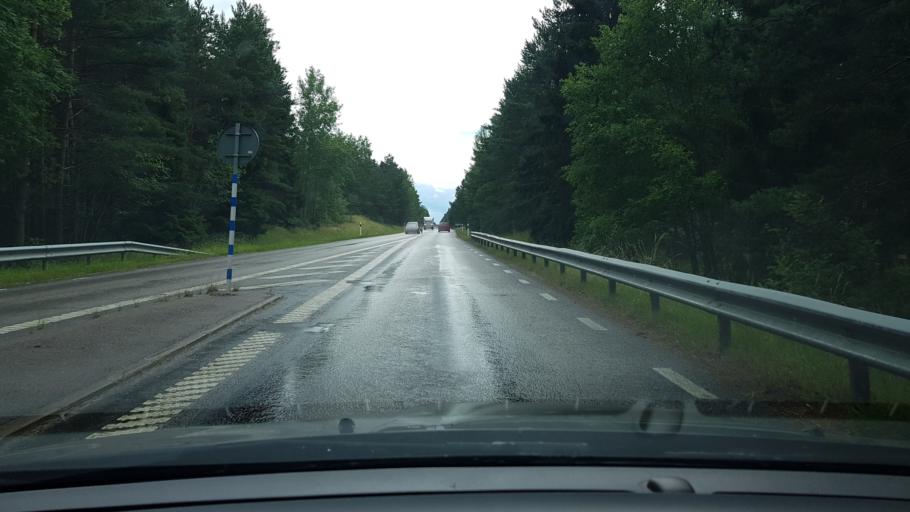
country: SE
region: Uppsala
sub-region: Uppsala Kommun
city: Saevja
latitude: 59.8076
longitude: 17.6882
